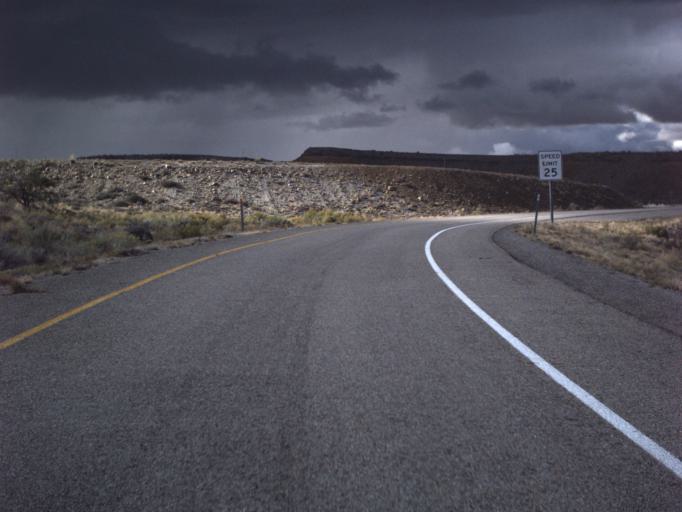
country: US
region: Utah
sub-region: Emery County
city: Castle Dale
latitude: 38.9377
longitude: -110.4798
